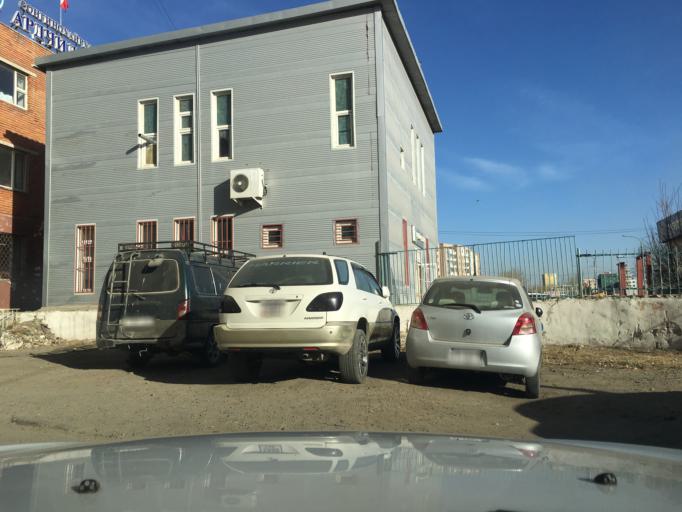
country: MN
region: Ulaanbaatar
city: Ulaanbaatar
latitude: 47.9125
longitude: 106.8437
